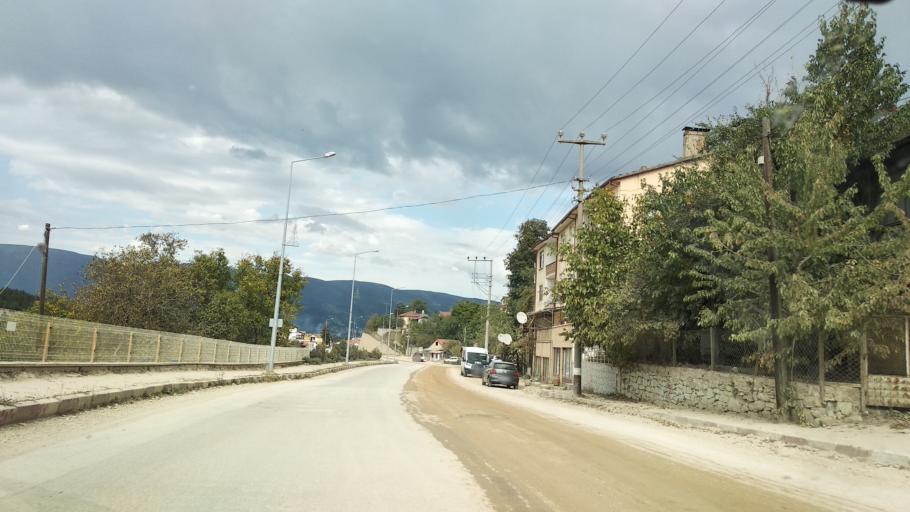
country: TR
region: Bolu
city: Mudurnu
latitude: 40.4709
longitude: 31.2099
